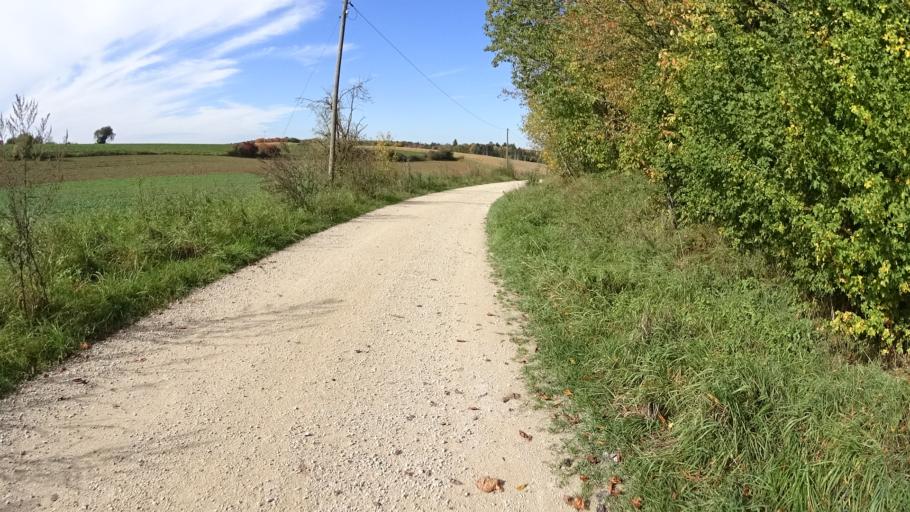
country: DE
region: Bavaria
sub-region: Upper Bavaria
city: Bohmfeld
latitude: 48.8636
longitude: 11.3744
